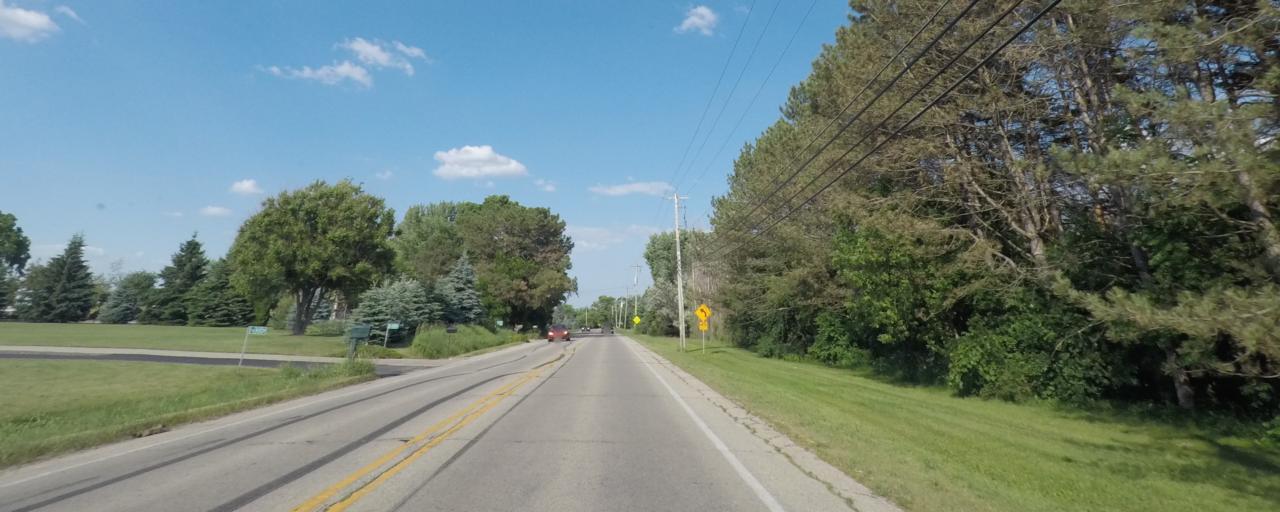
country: US
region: Wisconsin
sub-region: Waukesha County
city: Big Bend
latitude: 42.8629
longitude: -88.2324
